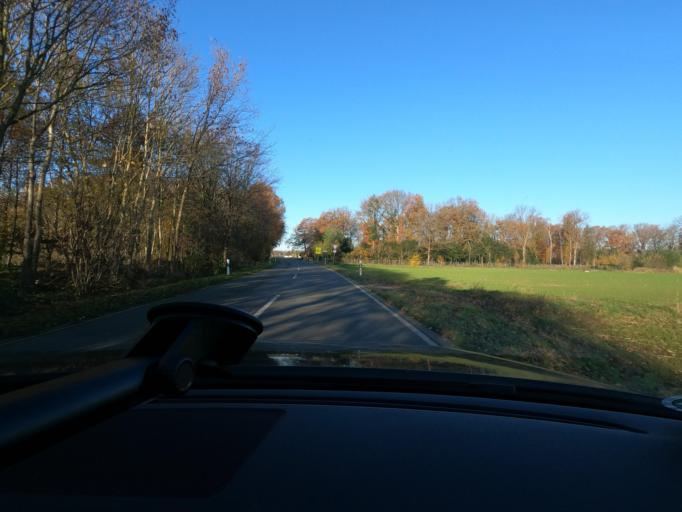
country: DE
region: North Rhine-Westphalia
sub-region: Regierungsbezirk Dusseldorf
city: Wachtendonk
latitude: 51.4395
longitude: 6.3400
